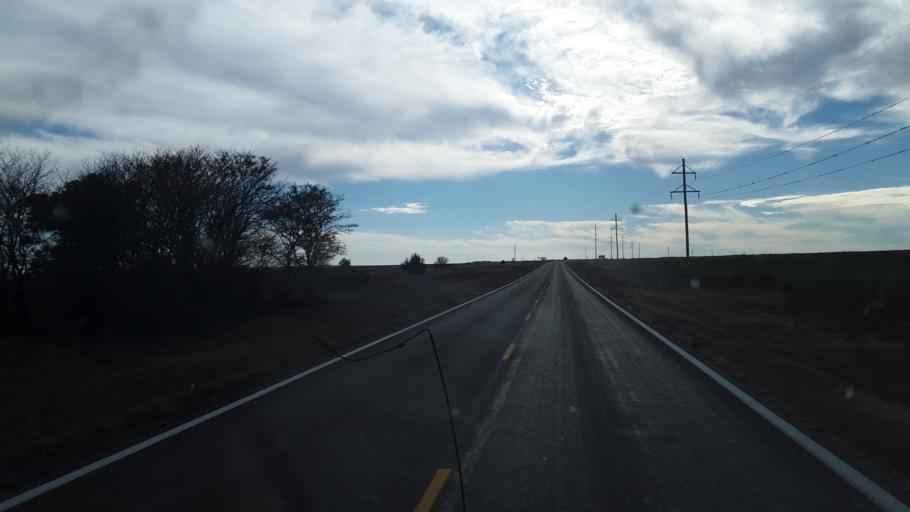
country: US
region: Kansas
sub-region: Hodgeman County
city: Jetmore
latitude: 38.1042
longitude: -99.7377
